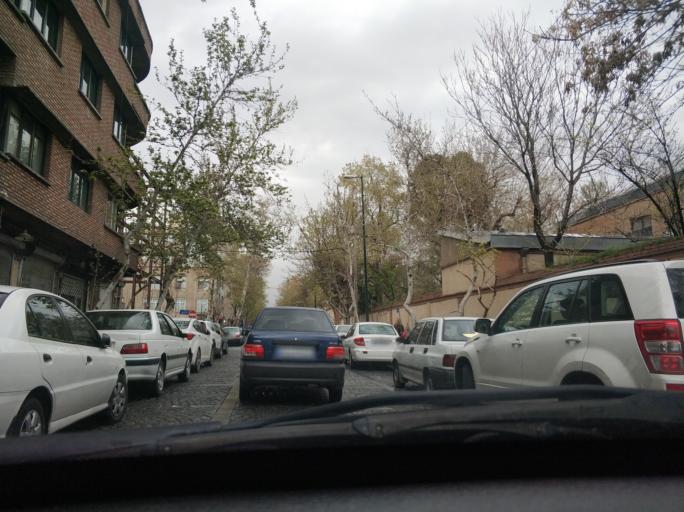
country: IR
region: Tehran
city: Tehran
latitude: 35.6911
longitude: 51.4143
